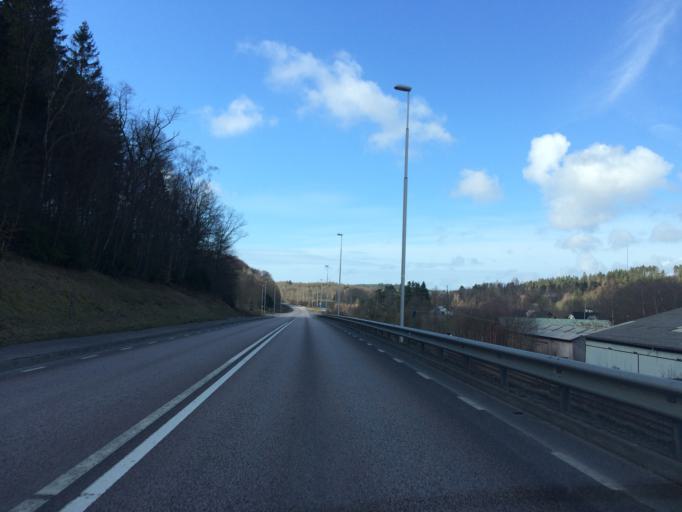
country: SE
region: Halland
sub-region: Laholms Kommun
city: Knared
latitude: 56.5145
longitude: 13.3146
